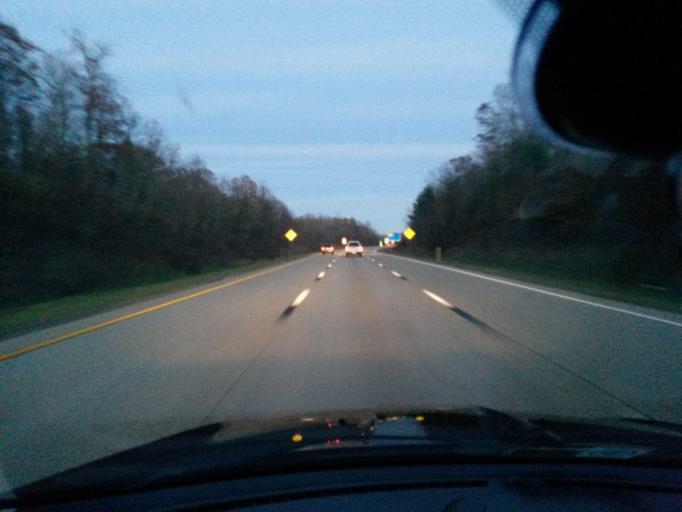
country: US
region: West Virginia
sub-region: Raleigh County
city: Daniels
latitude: 37.7736
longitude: -81.0978
